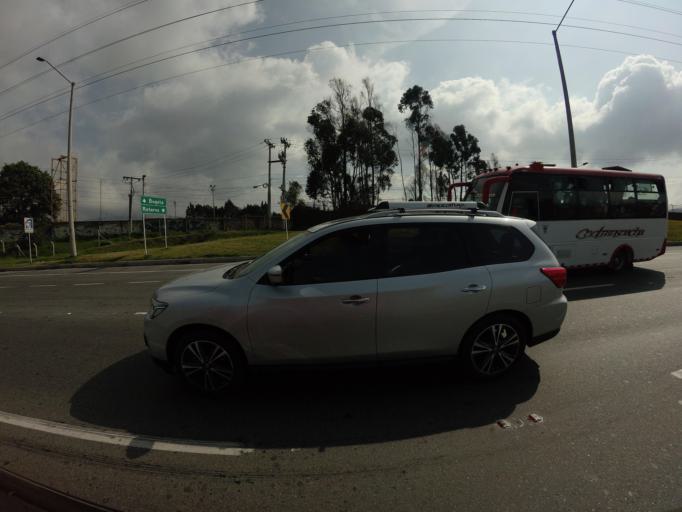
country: CO
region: Cundinamarca
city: Soacha
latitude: 4.5414
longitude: -74.2479
